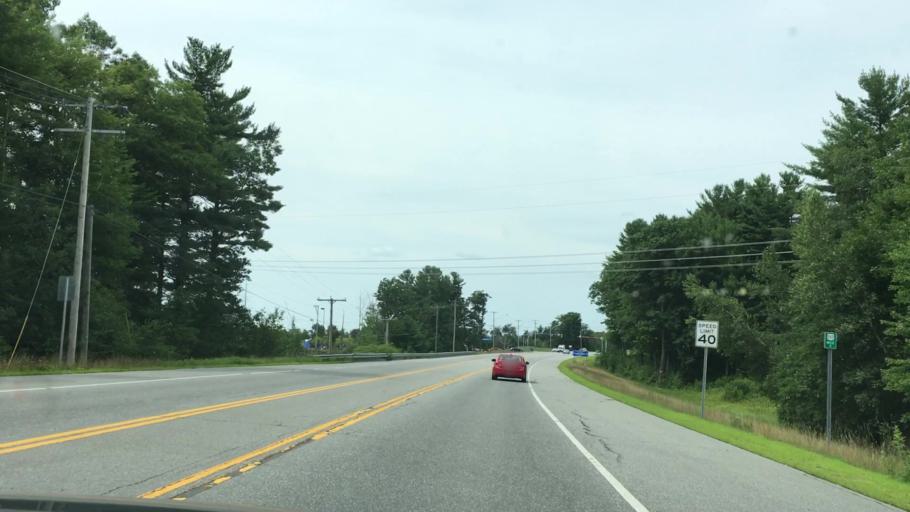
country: US
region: New Hampshire
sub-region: Cheshire County
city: Rindge
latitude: 42.7391
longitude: -72.0359
